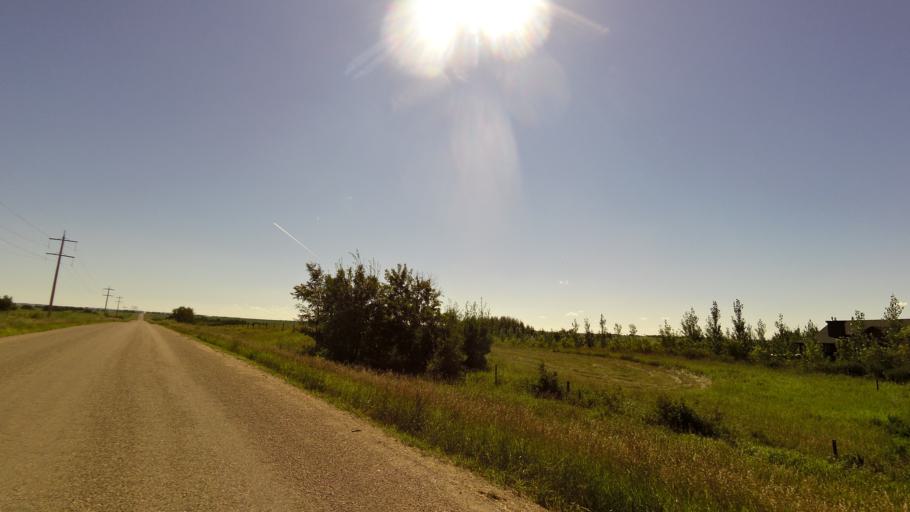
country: CA
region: Alberta
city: Wainwright
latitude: 52.8725
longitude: -111.0193
